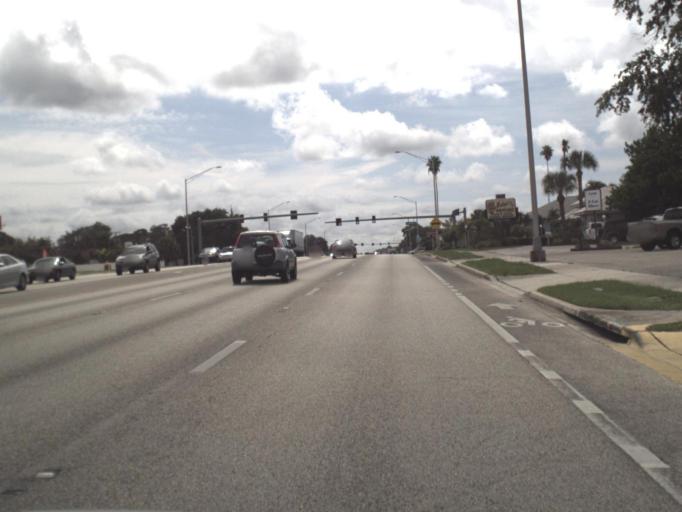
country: US
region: Florida
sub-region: Manatee County
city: Whitfield
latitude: 27.4107
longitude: -82.5715
